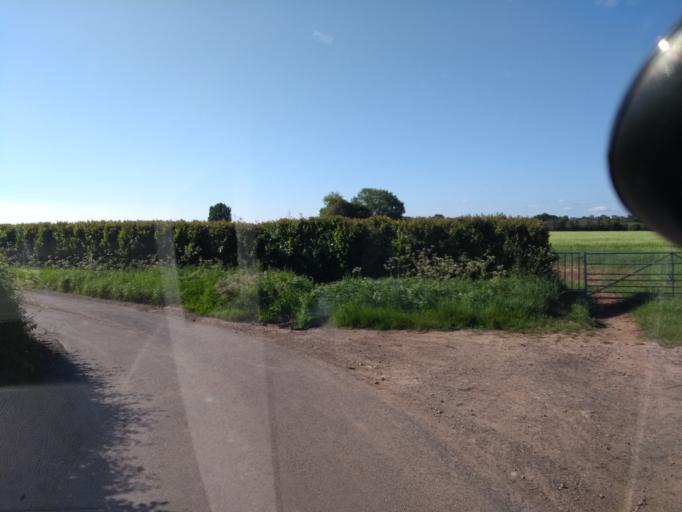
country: GB
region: England
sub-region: Somerset
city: Bridgwater
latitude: 51.1463
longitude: -3.0255
